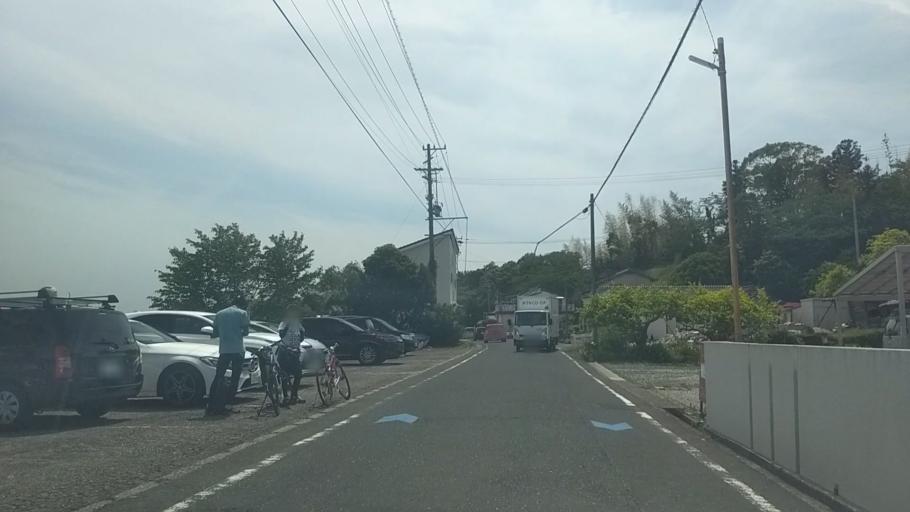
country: JP
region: Shizuoka
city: Kosai-shi
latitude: 34.7811
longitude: 137.5713
